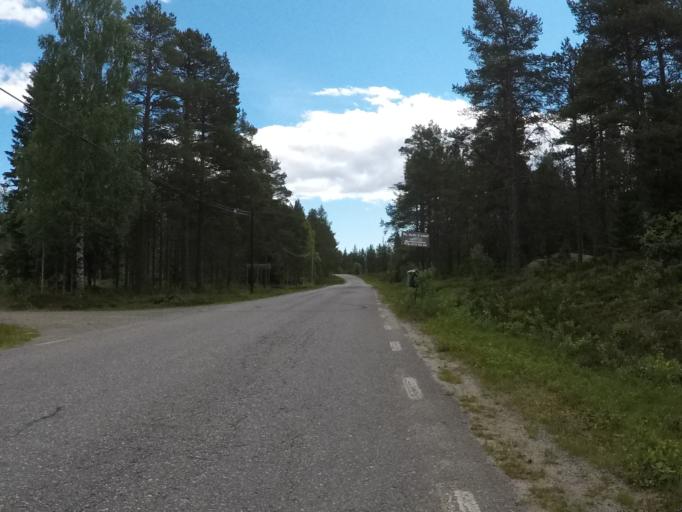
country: SE
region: Vaesterbotten
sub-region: Robertsfors Kommun
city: Robertsfors
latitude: 63.9940
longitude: 20.8184
